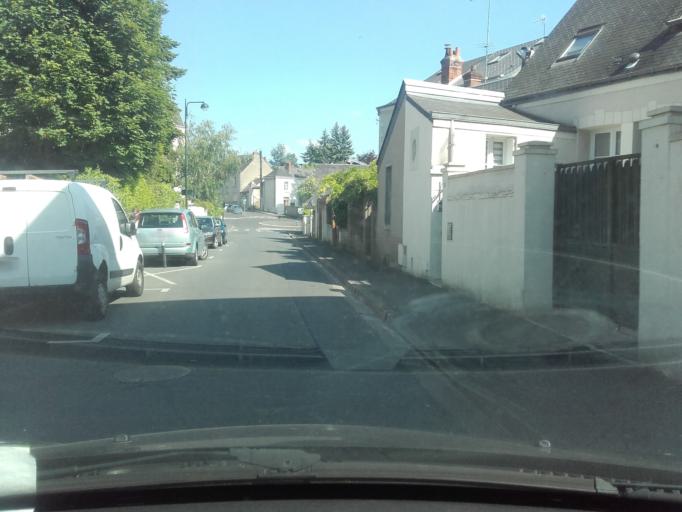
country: FR
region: Centre
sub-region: Departement d'Indre-et-Loire
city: Saint-Cyr-sur-Loire
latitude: 47.4079
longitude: 0.6782
